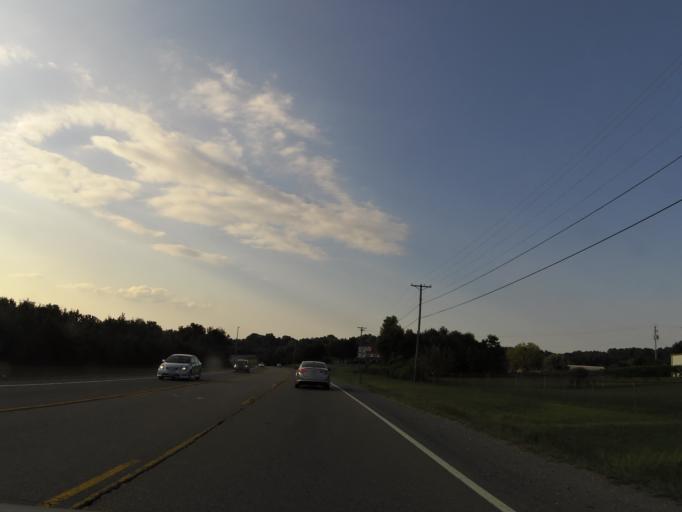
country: US
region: Tennessee
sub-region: Knox County
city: Knoxville
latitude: 35.9828
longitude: -83.8255
